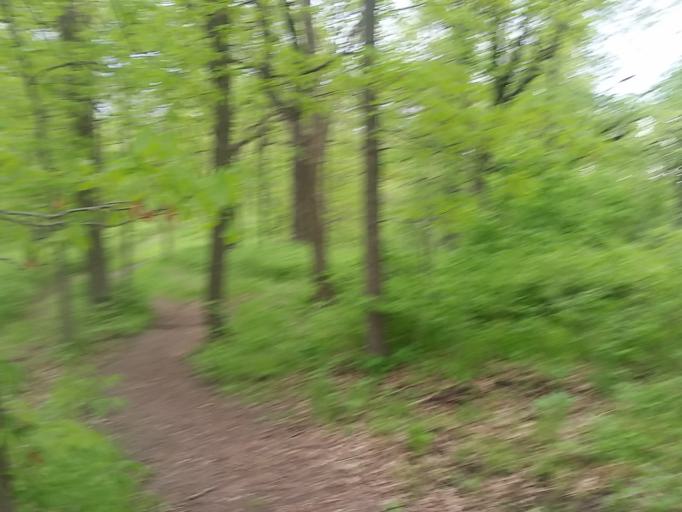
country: US
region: Nebraska
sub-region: Sarpy County
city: Bellevue
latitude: 41.1796
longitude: -95.9086
